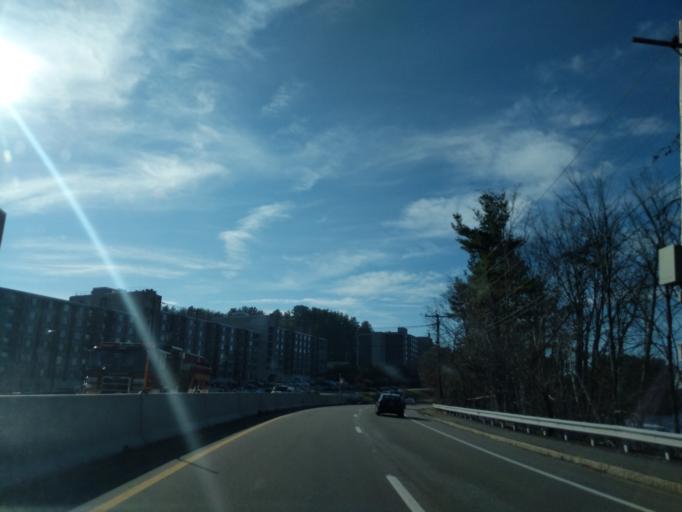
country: US
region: Massachusetts
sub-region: Middlesex County
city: Framingham Center
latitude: 42.2935
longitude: -71.4596
